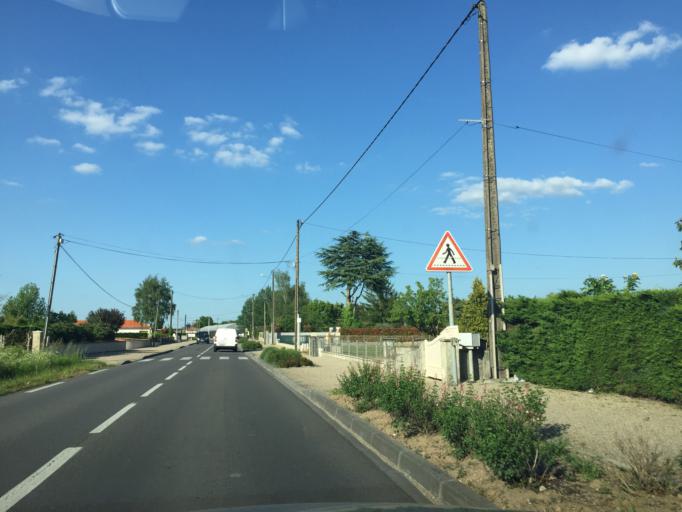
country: FR
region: Aquitaine
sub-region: Departement de la Gironde
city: Les Peintures
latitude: 45.0631
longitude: -0.0981
